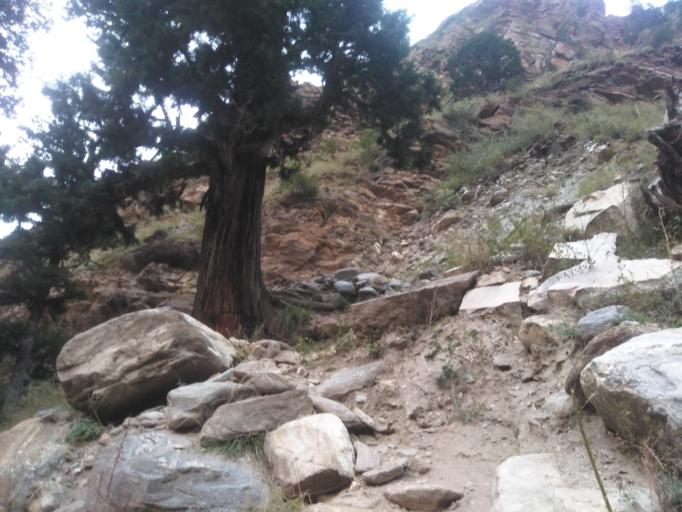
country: NP
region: Western Region
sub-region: Dhawalagiri Zone
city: Jomsom
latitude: 28.8818
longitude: 83.0235
